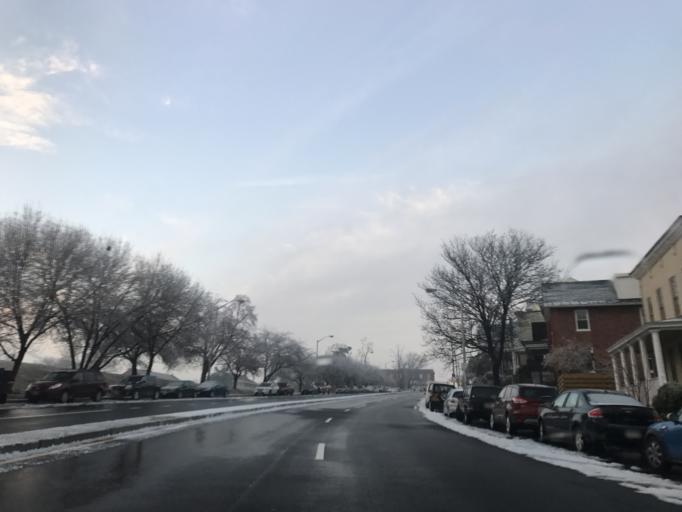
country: US
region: Maryland
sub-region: City of Baltimore
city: Baltimore
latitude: 39.3285
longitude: -76.6341
